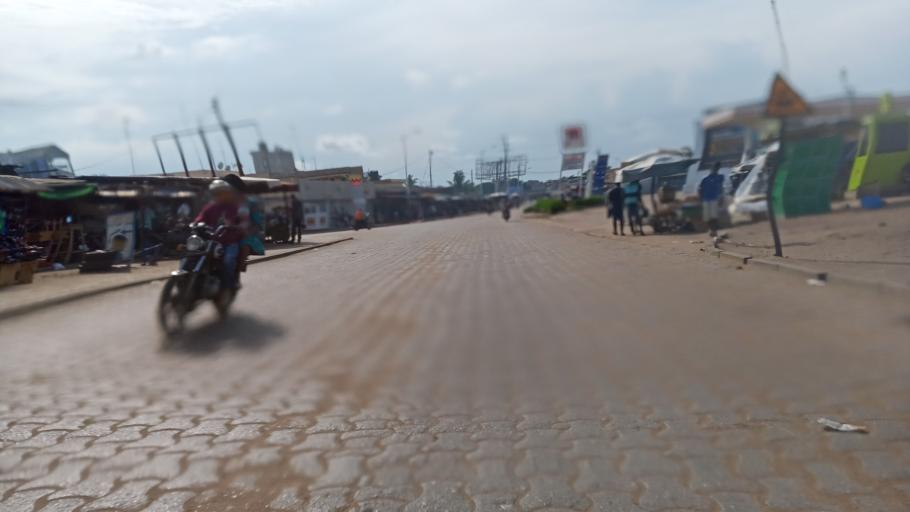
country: TG
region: Maritime
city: Lome
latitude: 6.1550
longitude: 1.2678
